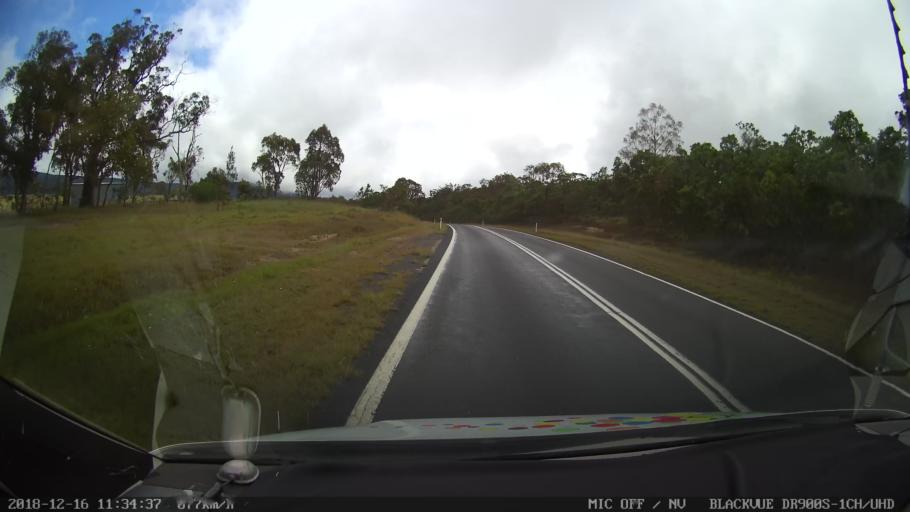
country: AU
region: New South Wales
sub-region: Tenterfield Municipality
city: Carrolls Creek
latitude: -28.9978
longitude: 152.1560
